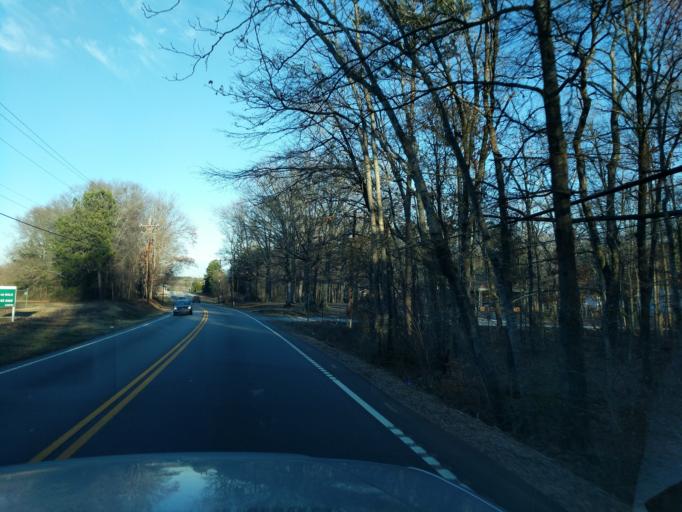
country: US
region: South Carolina
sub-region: Greenville County
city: Fountain Inn
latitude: 34.6756
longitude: -82.2131
